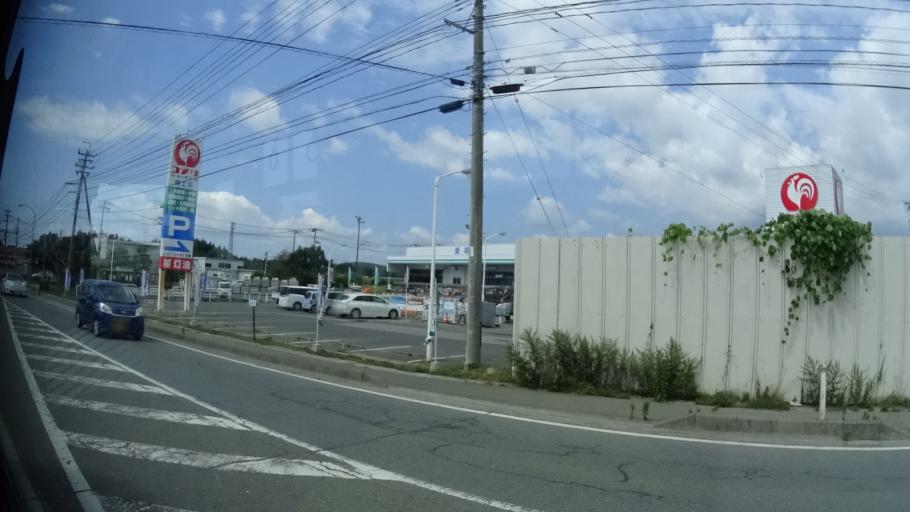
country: JP
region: Iwate
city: Ofunato
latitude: 38.8327
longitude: 141.5779
